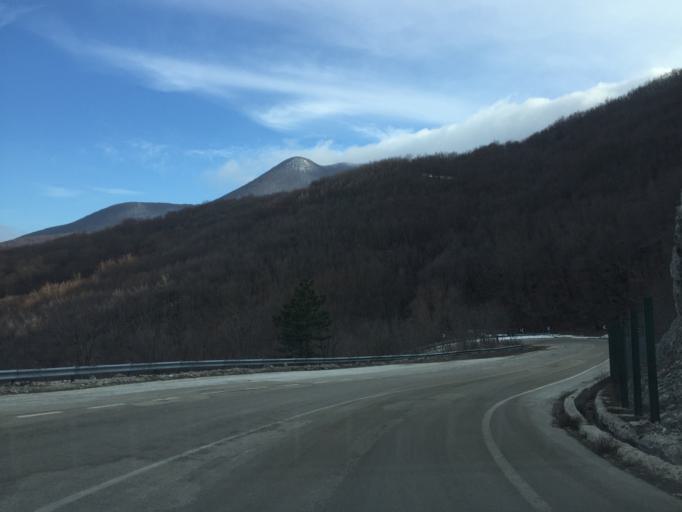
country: IT
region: Molise
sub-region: Provincia di Campobasso
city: San Massimo
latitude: 41.4747
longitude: 14.4171
